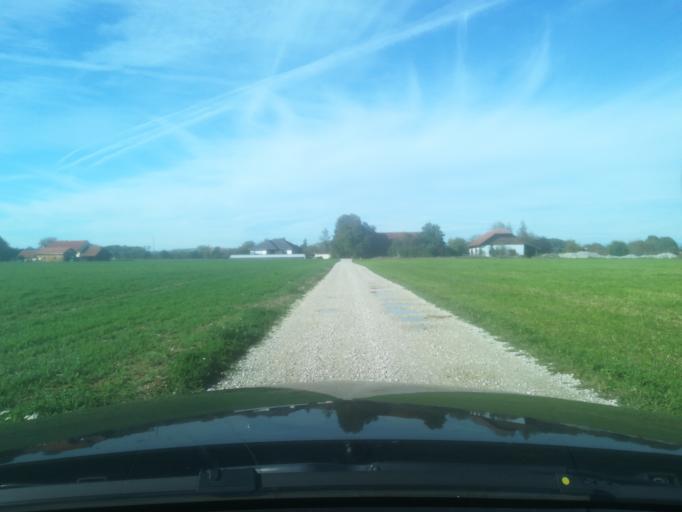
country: AT
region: Upper Austria
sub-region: Politischer Bezirk Linz-Land
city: Horsching
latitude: 48.2059
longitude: 14.1505
